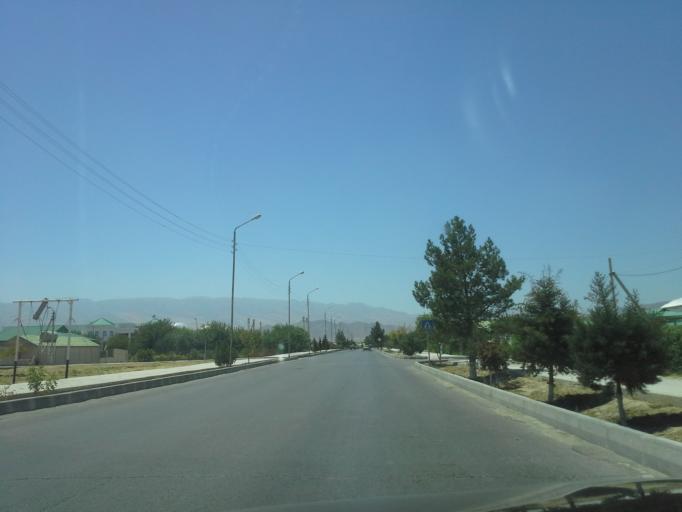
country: TM
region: Ahal
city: Abadan
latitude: 38.0303
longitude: 58.2645
